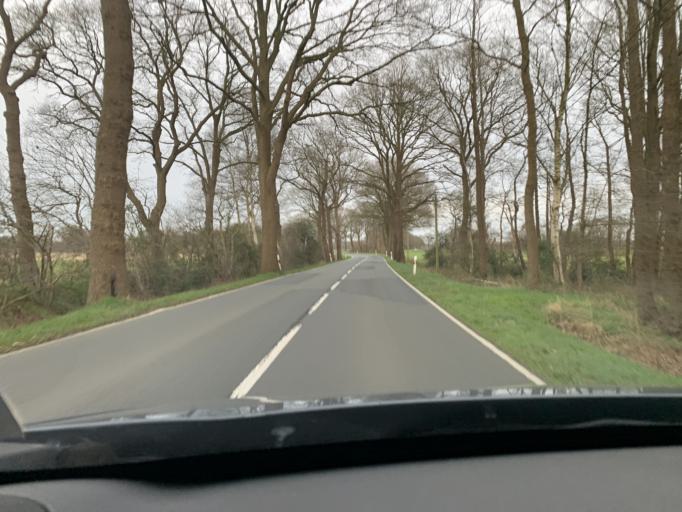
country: DE
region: Lower Saxony
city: Apen
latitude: 53.1792
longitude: 7.7914
